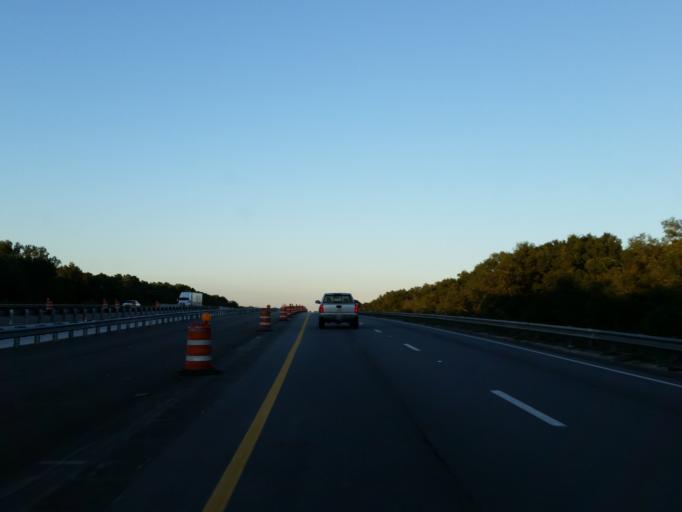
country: US
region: Florida
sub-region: Hernando County
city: Ridge Manor
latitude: 28.5907
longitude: -82.2083
